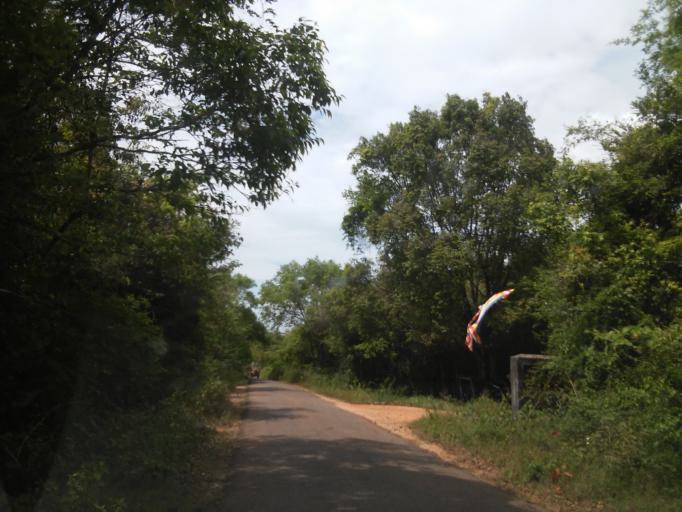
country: LK
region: Central
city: Sigiriya
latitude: 8.1061
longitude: 80.6793
